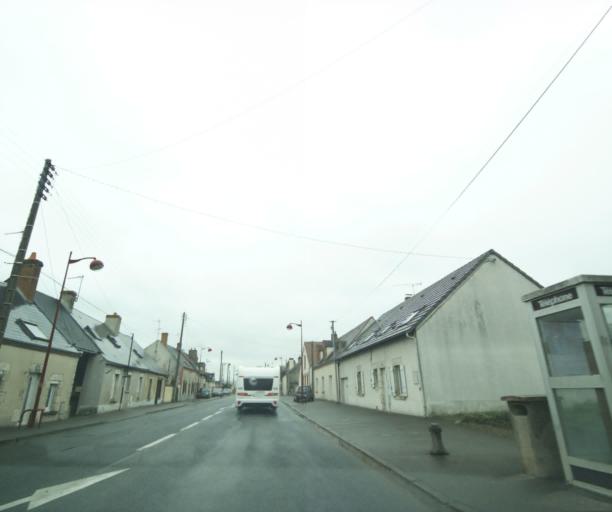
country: FR
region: Centre
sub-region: Departement du Loiret
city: Saran
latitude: 47.9836
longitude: 1.8830
